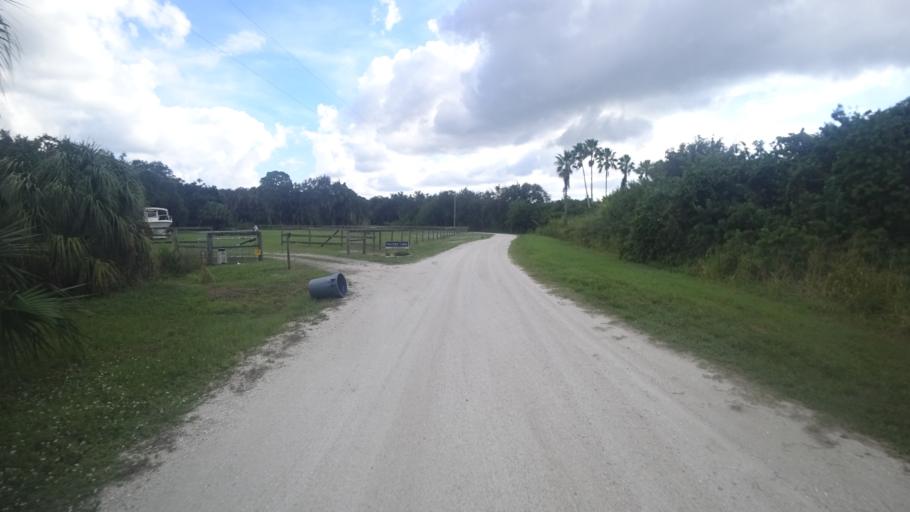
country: US
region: Florida
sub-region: Manatee County
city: Memphis
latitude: 27.6198
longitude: -82.5150
